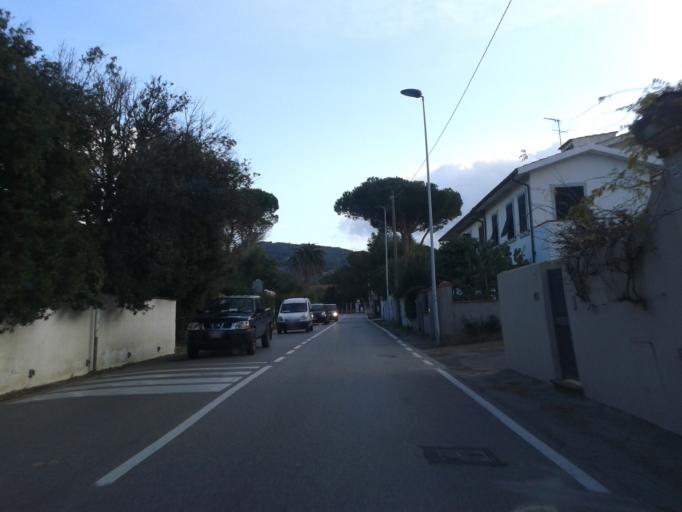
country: IT
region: Tuscany
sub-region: Provincia di Livorno
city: Livorno
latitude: 43.5044
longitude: 10.3383
